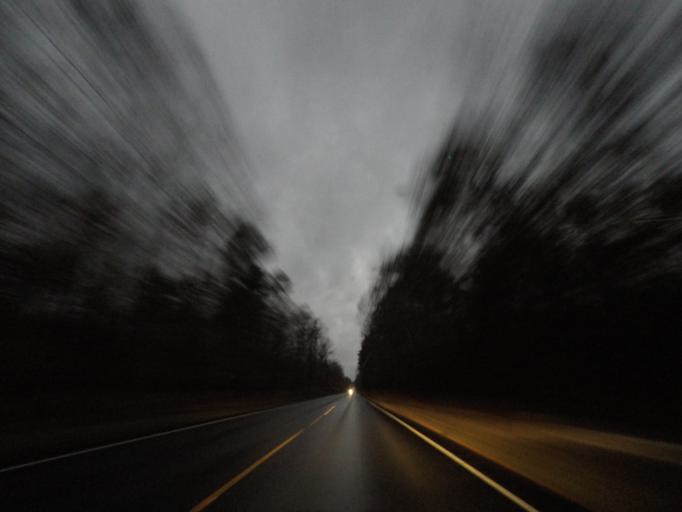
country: US
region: North Carolina
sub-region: Orange County
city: Hillsborough
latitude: 36.0505
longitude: -79.0329
